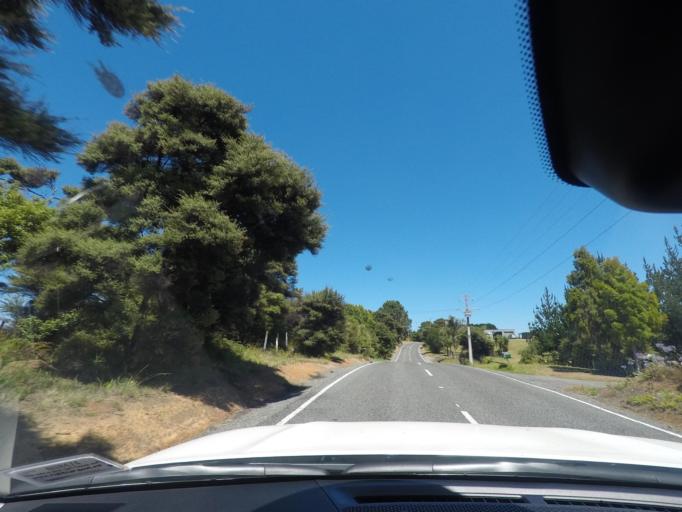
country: NZ
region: Auckland
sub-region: Auckland
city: Parakai
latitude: -36.5770
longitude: 174.3421
